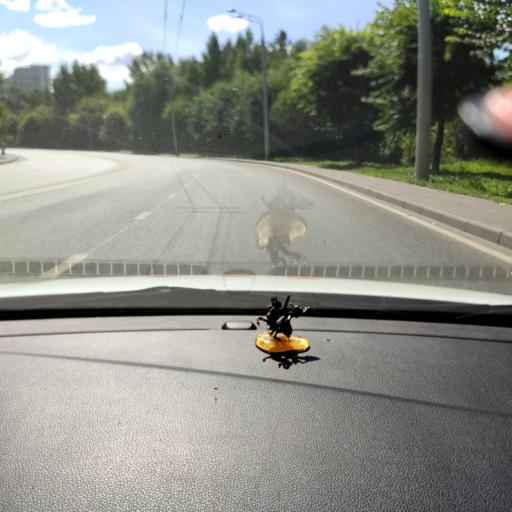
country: RU
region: Tatarstan
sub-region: Gorod Kazan'
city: Kazan
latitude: 55.7417
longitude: 49.1641
